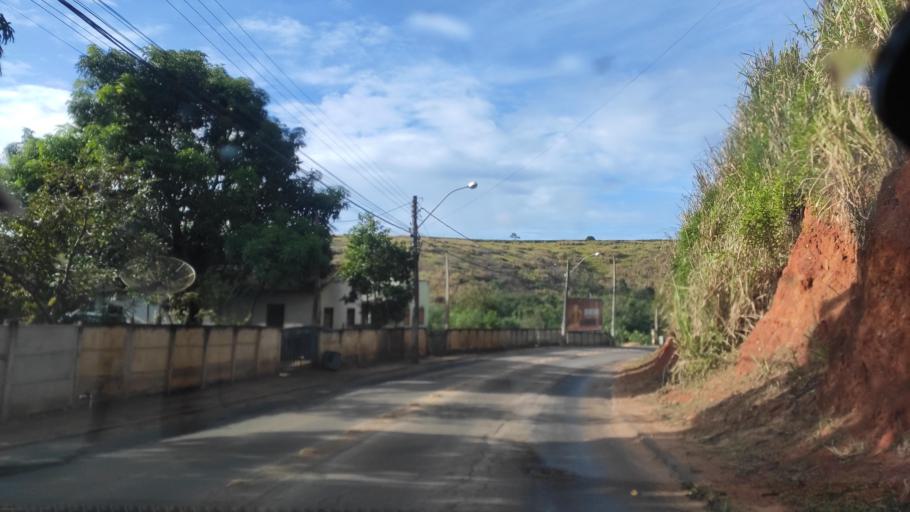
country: BR
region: Espirito Santo
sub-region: Nova Venecia
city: Nova Venecia
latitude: -18.7137
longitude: -40.3891
